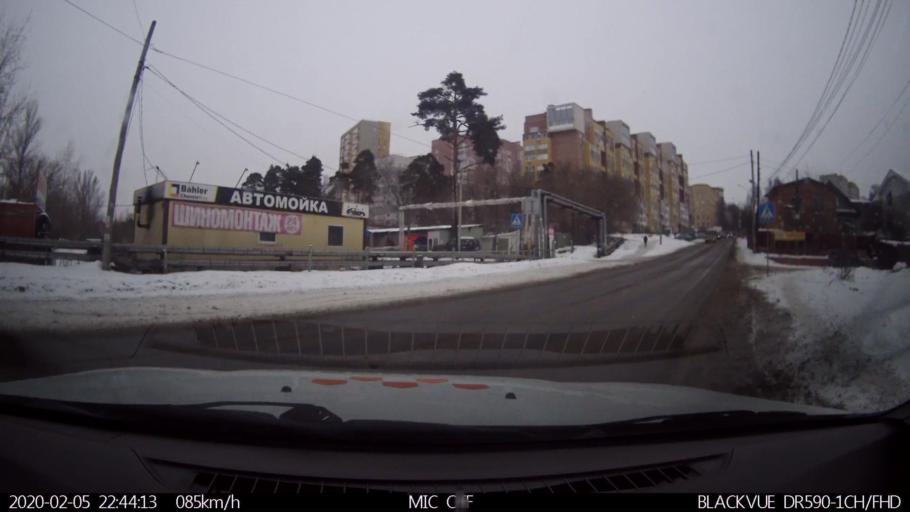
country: RU
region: Nizjnij Novgorod
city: Imeni Stepana Razina
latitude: 54.7096
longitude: 44.3976
